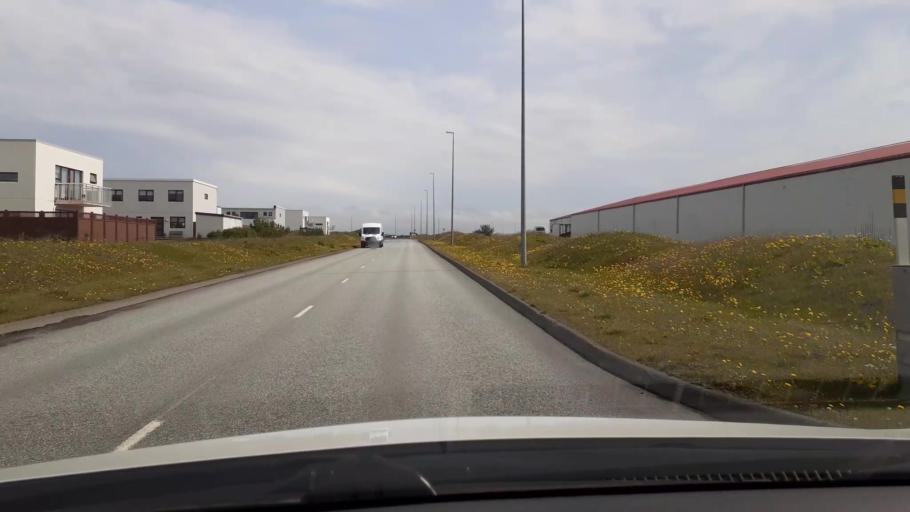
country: IS
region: Southern Peninsula
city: Reykjanesbaer
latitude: 63.9712
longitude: -22.5212
